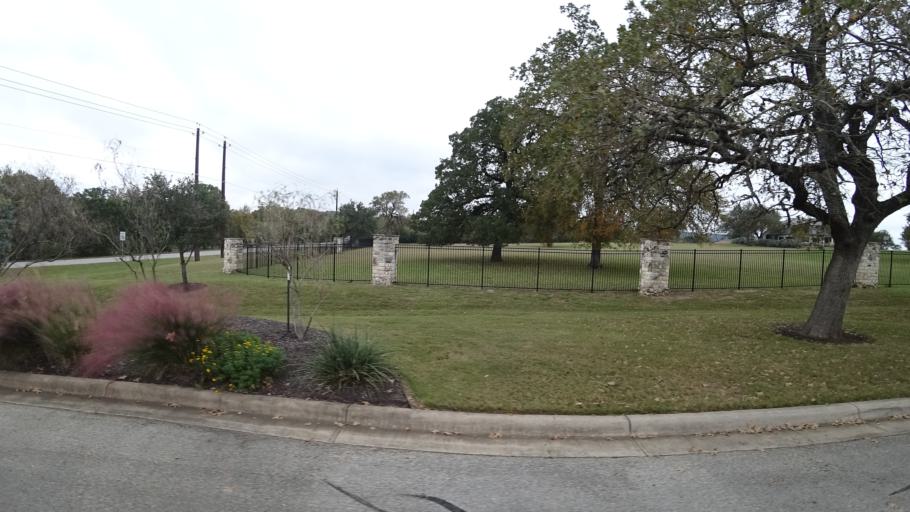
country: US
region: Texas
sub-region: Travis County
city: Bee Cave
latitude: 30.3348
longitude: -97.9231
